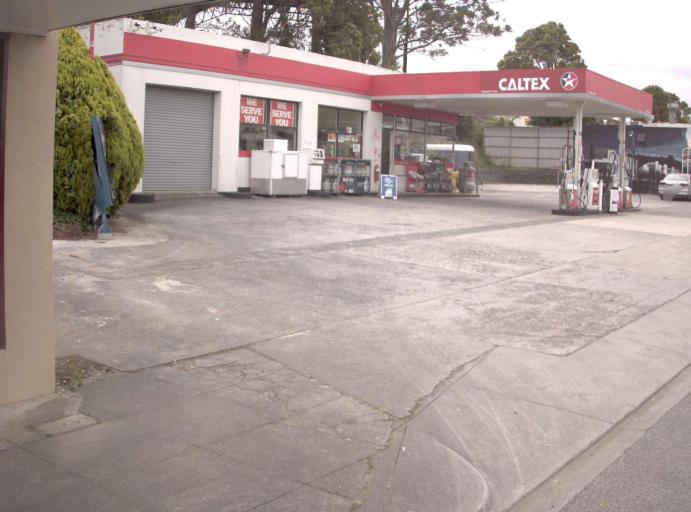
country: AU
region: Victoria
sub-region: Bass Coast
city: North Wonthaggi
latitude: -38.4311
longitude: 145.8230
